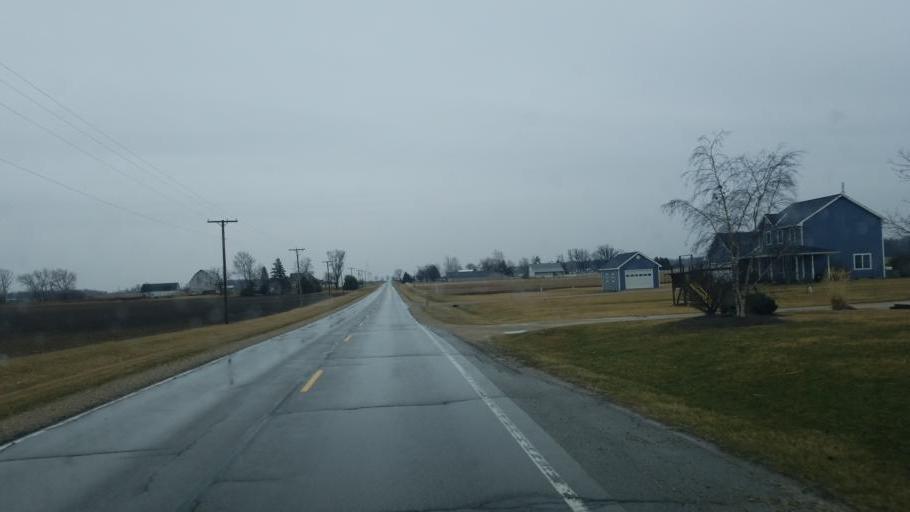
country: US
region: Indiana
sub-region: Adams County
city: Geneva
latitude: 40.6174
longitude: -85.0411
